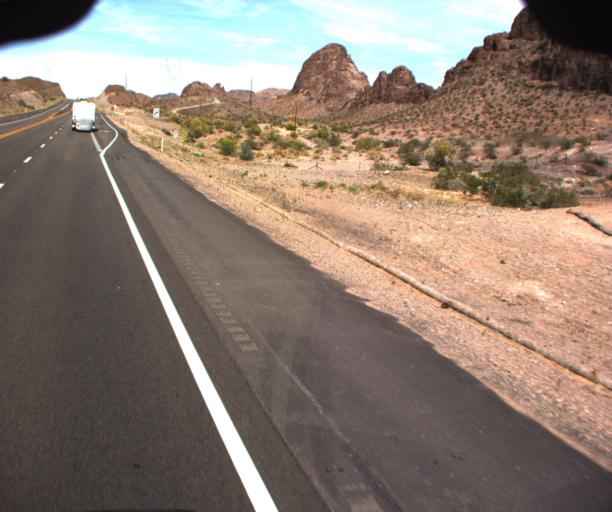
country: US
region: Arizona
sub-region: Mohave County
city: Desert Hills
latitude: 34.6086
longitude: -114.3576
